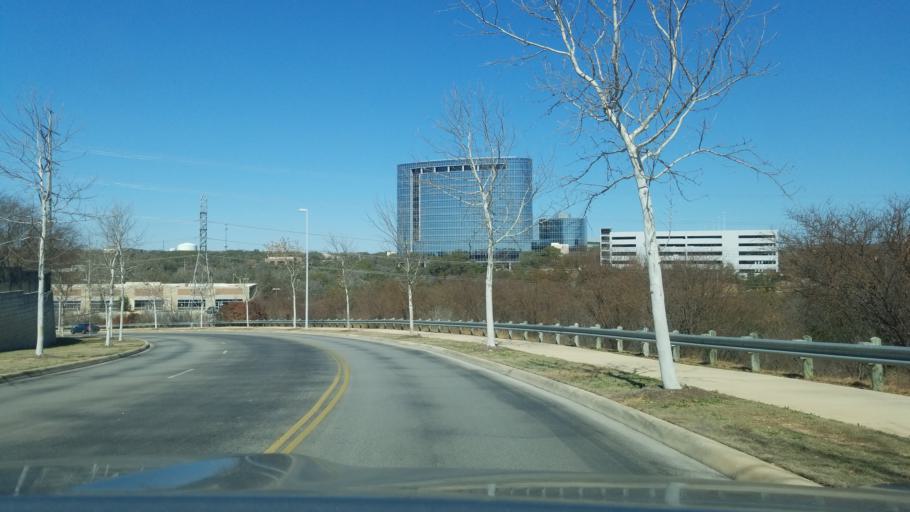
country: US
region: Texas
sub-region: Bexar County
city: Hollywood Park
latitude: 29.6130
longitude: -98.4621
